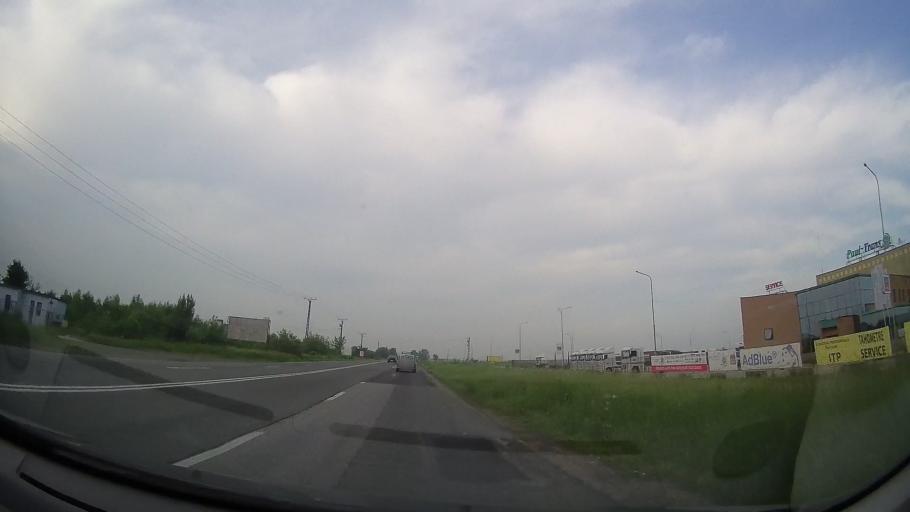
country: RO
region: Timis
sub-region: Comuna Giroc
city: Chisoda
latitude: 45.6957
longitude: 21.1780
